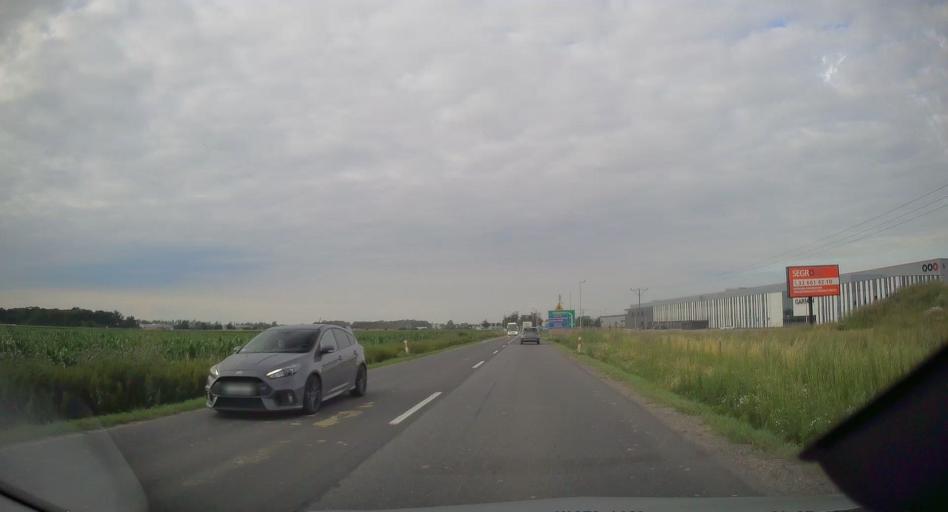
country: PL
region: Lower Silesian Voivodeship
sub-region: Powiat wroclawski
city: Tyniec Maly
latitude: 51.0334
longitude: 16.8904
